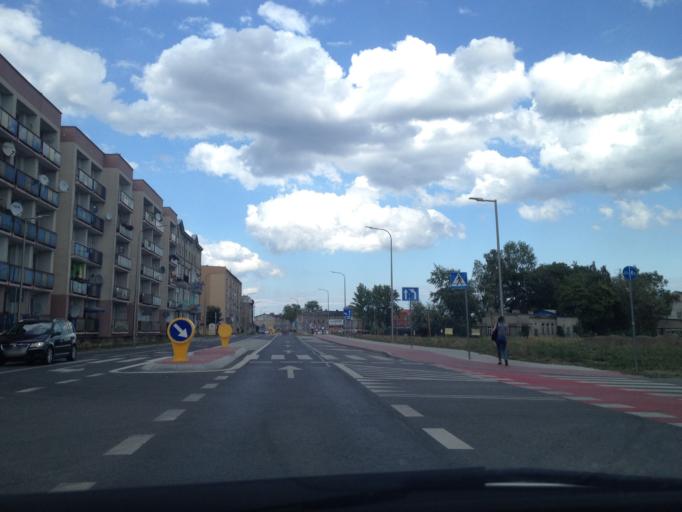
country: PL
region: Lubusz
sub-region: Powiat zarski
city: Zary
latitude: 51.6388
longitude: 15.1236
